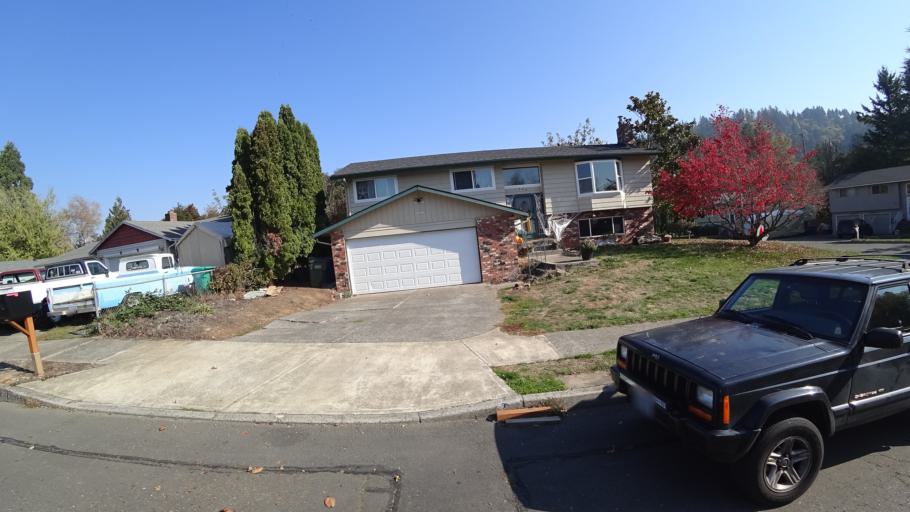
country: US
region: Oregon
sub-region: Multnomah County
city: Gresham
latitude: 45.4906
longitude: -122.4494
